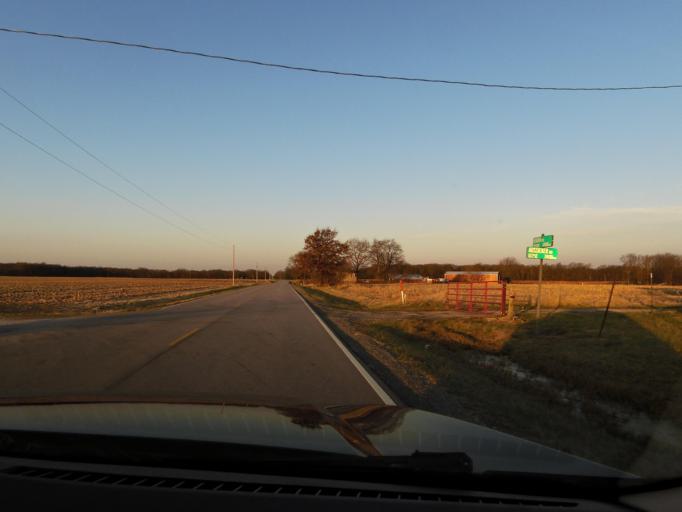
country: US
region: Illinois
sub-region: Marion County
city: Salem
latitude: 38.7588
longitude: -88.9149
